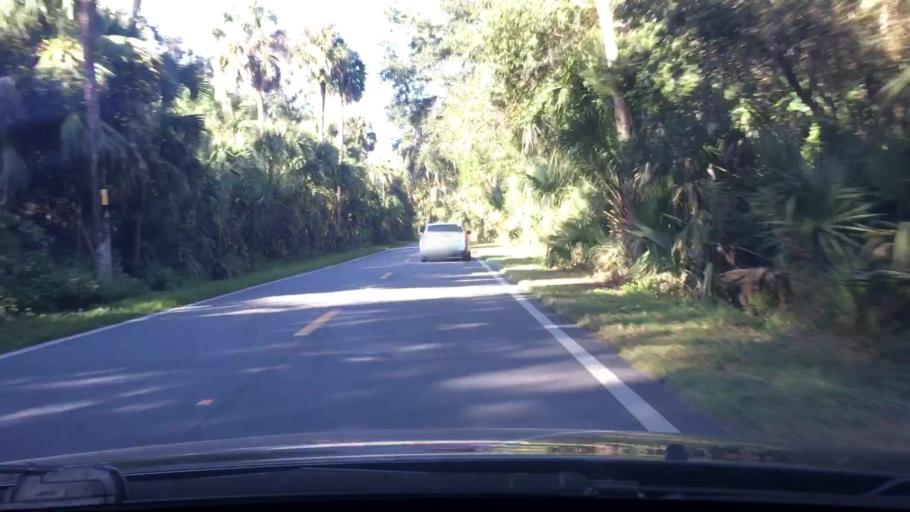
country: US
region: Florida
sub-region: Flagler County
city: Flagler Beach
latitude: 29.3983
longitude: -81.1358
